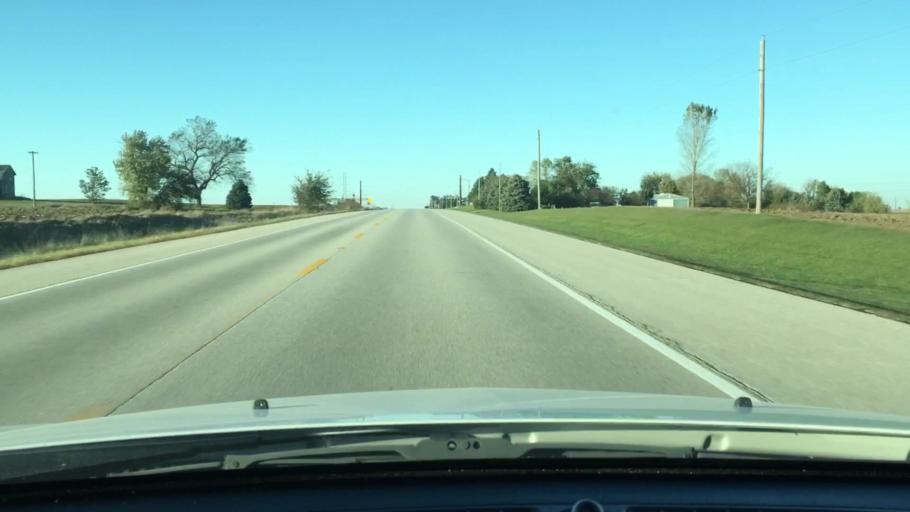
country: US
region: Illinois
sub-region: DeKalb County
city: Waterman
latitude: 41.8211
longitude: -88.7539
